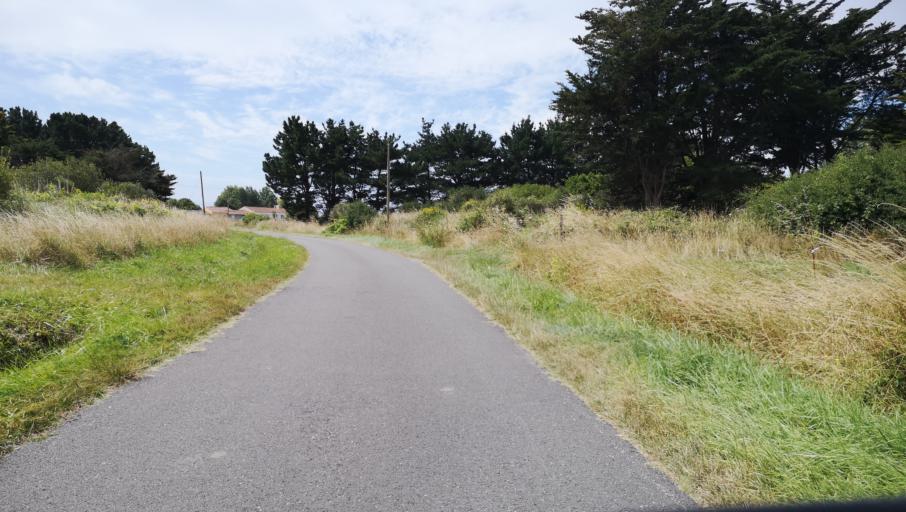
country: FR
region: Pays de la Loire
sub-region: Departement de la Vendee
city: Olonne-sur-Mer
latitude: 46.5271
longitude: -1.7990
